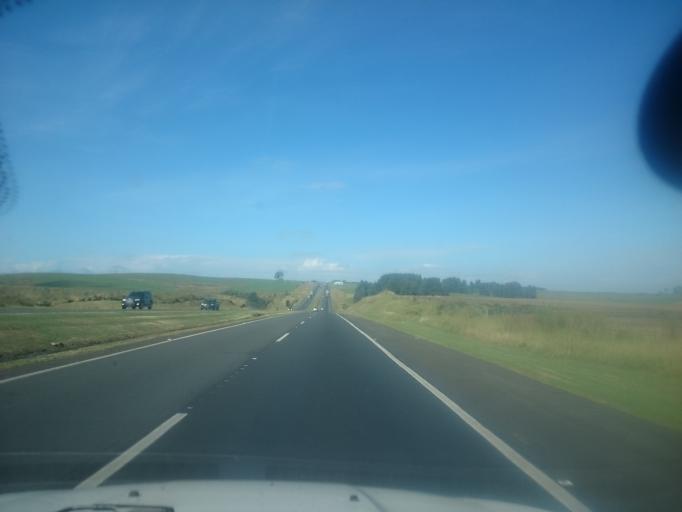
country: BR
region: Parana
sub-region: Palmeira
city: Palmeira
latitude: -25.3735
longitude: -49.8163
